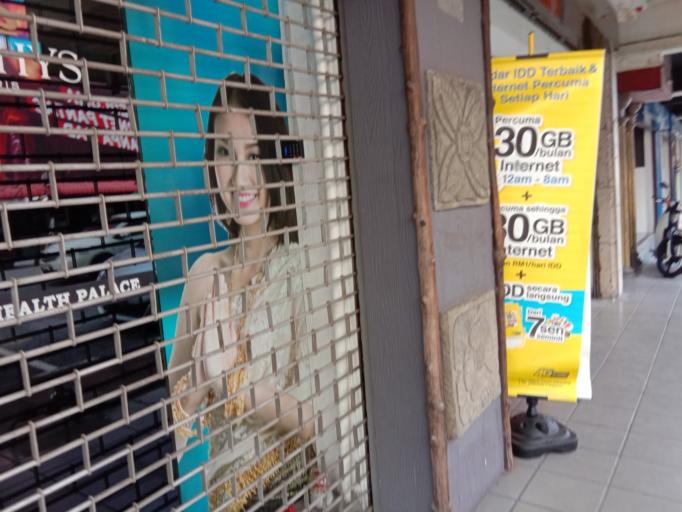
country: MY
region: Perak
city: Ipoh
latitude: 4.5991
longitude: 101.0840
